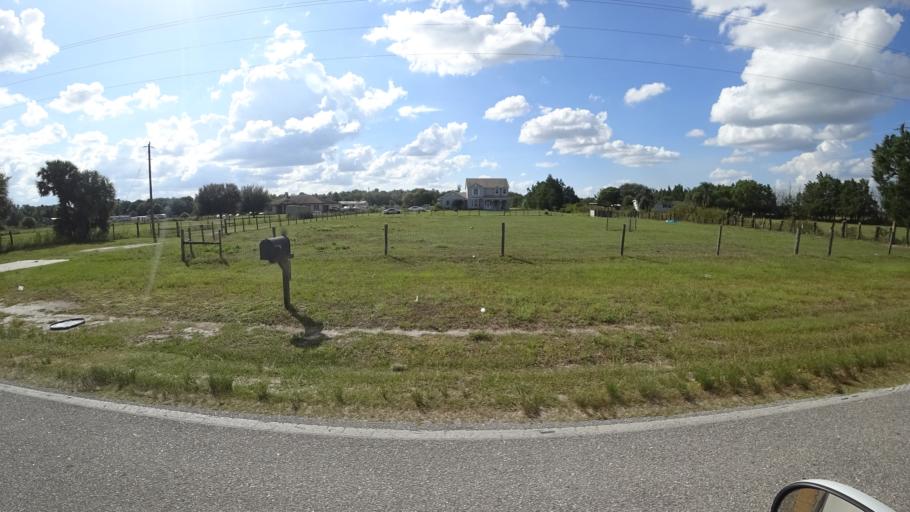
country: US
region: Florida
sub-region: DeSoto County
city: Nocatee
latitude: 27.2914
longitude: -82.1134
